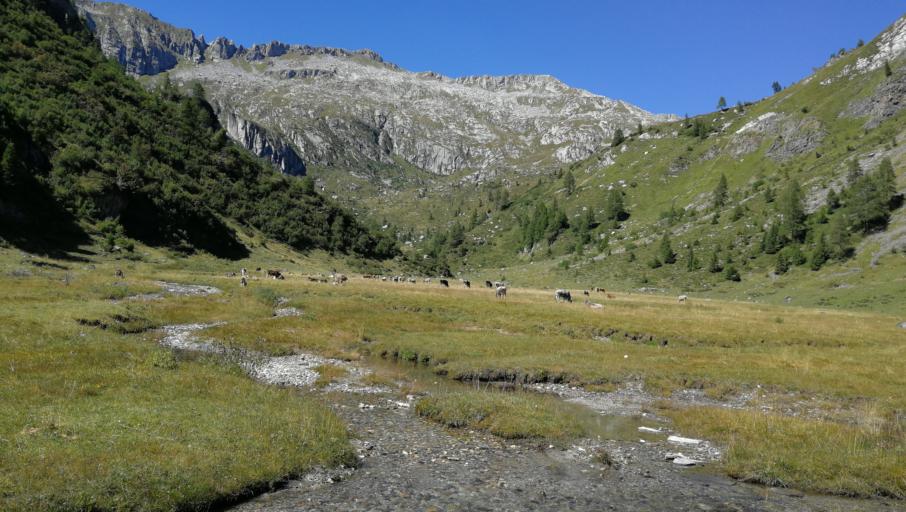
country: IT
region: Trentino-Alto Adige
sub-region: Provincia di Trento
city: Brione
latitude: 45.9292
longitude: 10.5165
